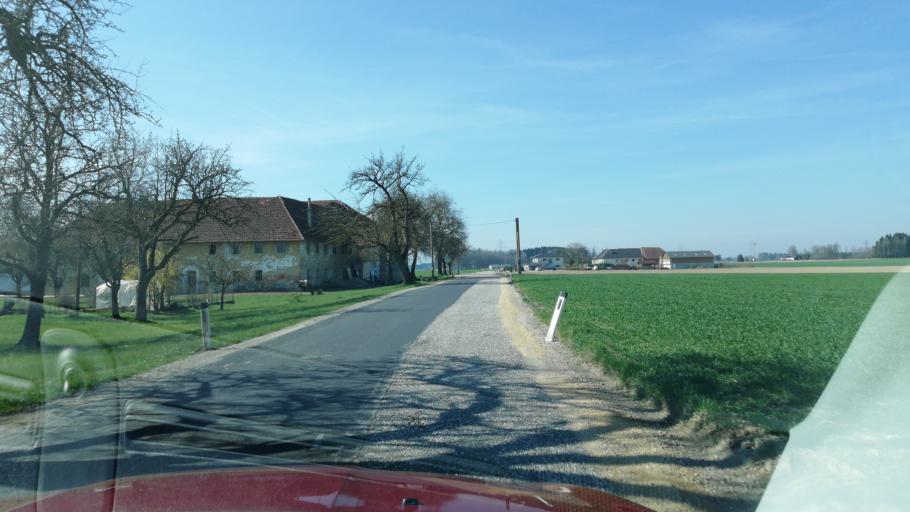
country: AT
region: Upper Austria
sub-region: Politischer Bezirk Kirchdorf an der Krems
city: Kremsmunster
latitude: 48.0932
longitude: 14.0997
